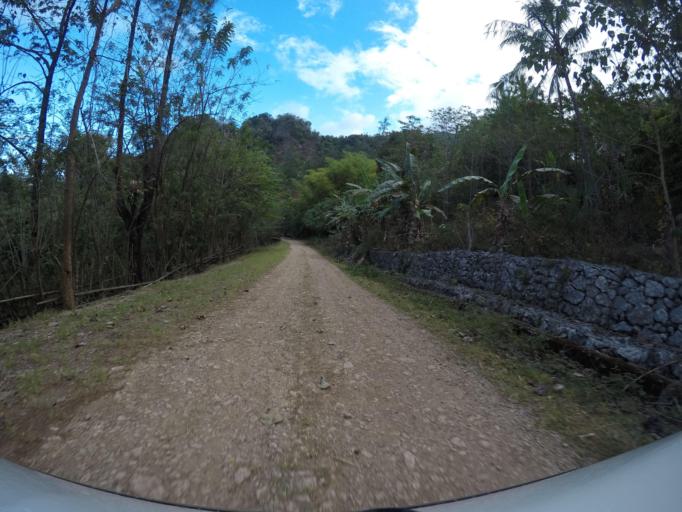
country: TL
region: Baucau
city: Venilale
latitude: -8.6845
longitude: 126.6535
